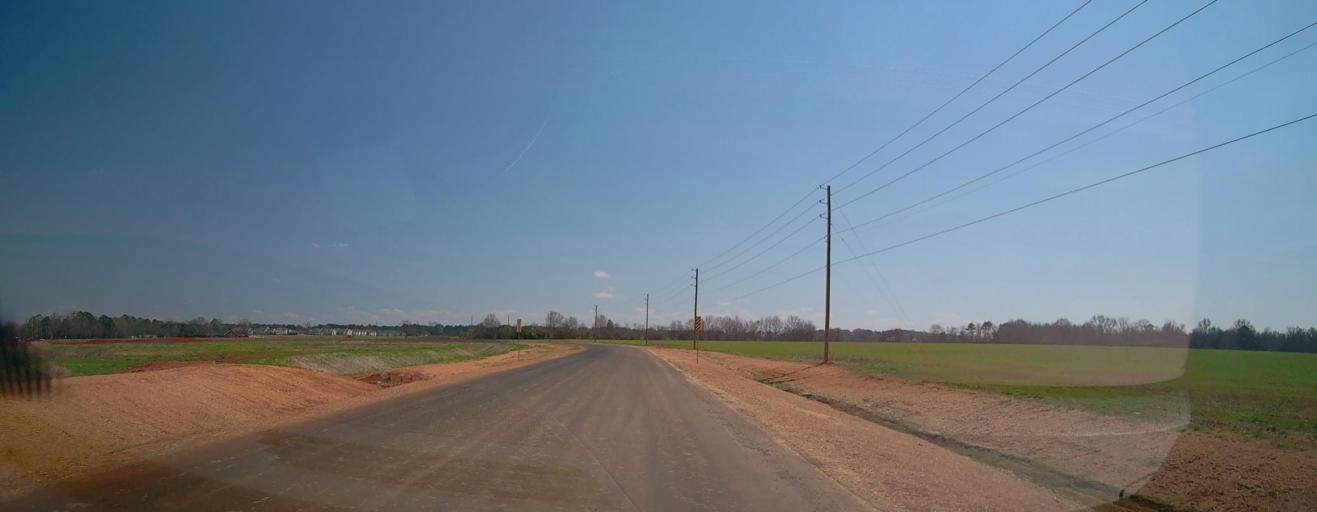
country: US
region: Georgia
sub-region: Houston County
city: Centerville
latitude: 32.5975
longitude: -83.7274
